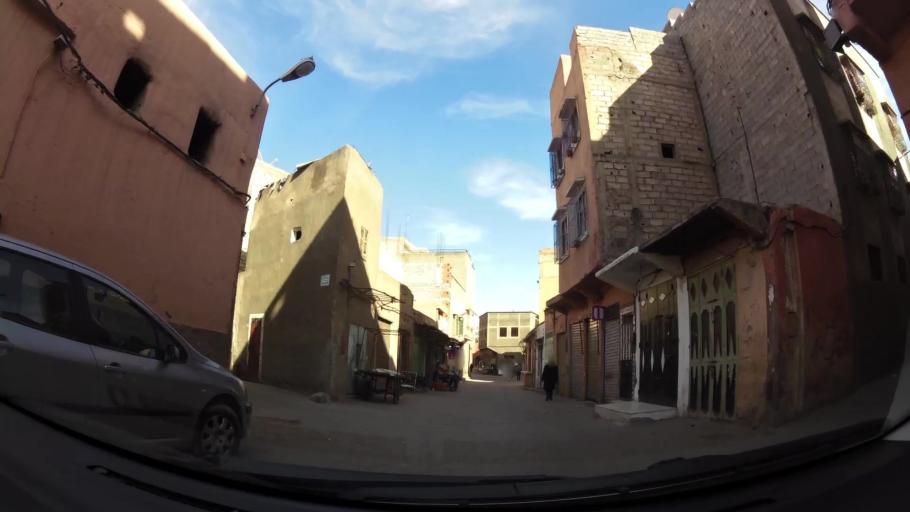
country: MA
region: Marrakech-Tensift-Al Haouz
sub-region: Marrakech
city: Marrakesh
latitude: 31.6162
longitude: -7.9660
